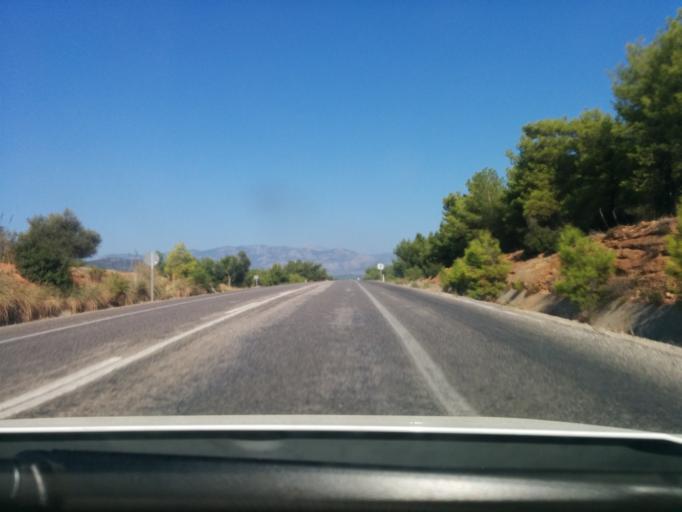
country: TR
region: Mugla
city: Esen
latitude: 36.3678
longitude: 29.3274
